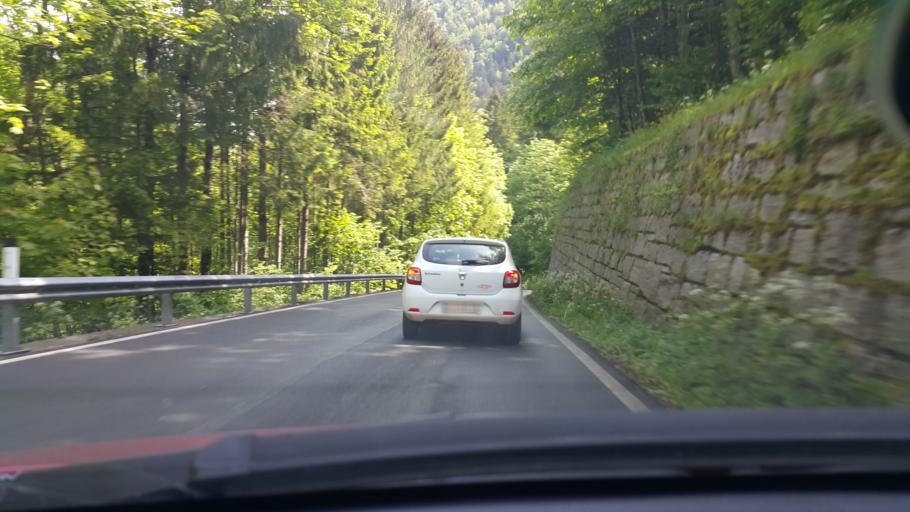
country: AT
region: Carinthia
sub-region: Politischer Bezirk Klagenfurt Land
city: Ferlach
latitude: 46.4803
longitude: 14.2569
